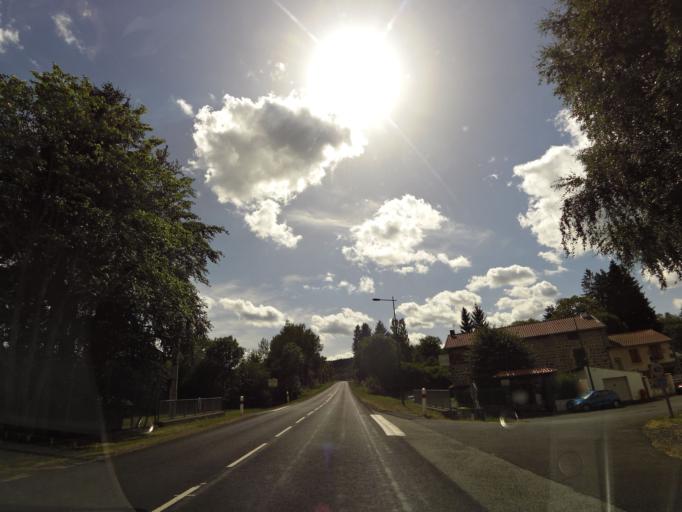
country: FR
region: Auvergne
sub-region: Departement du Puy-de-Dome
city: Orcines
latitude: 45.7651
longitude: 2.9977
